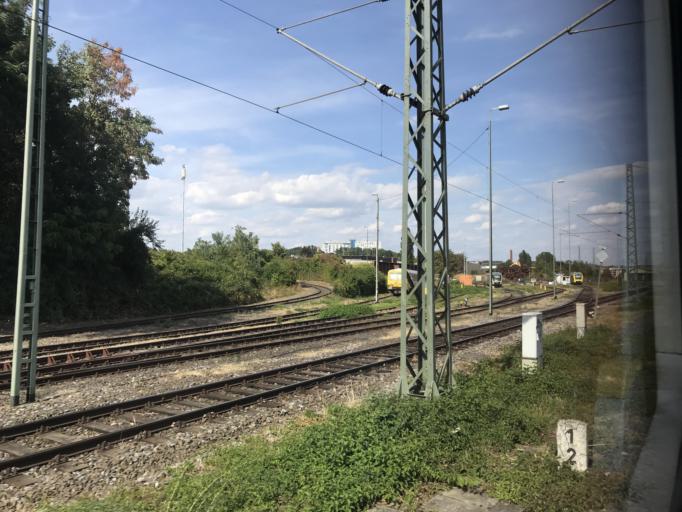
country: DE
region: Hesse
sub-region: Regierungsbezirk Giessen
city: Limburg an der Lahn
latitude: 50.3776
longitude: 8.0503
